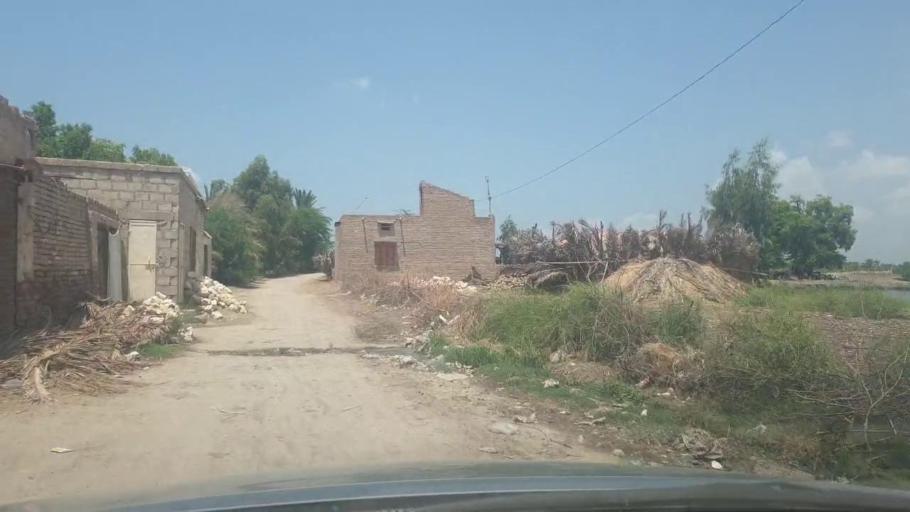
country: PK
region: Sindh
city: Kot Diji
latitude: 27.4211
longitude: 68.7374
